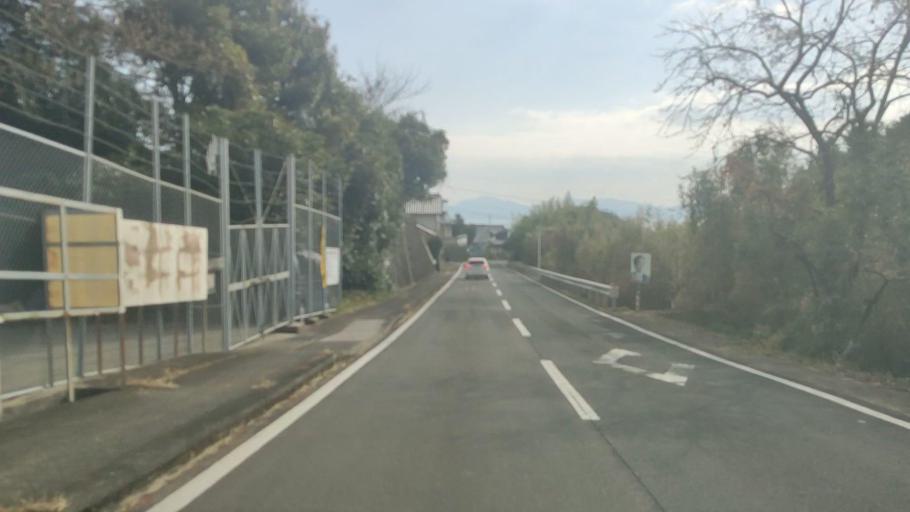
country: JP
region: Nagasaki
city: Shimabara
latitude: 32.6753
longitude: 130.2814
